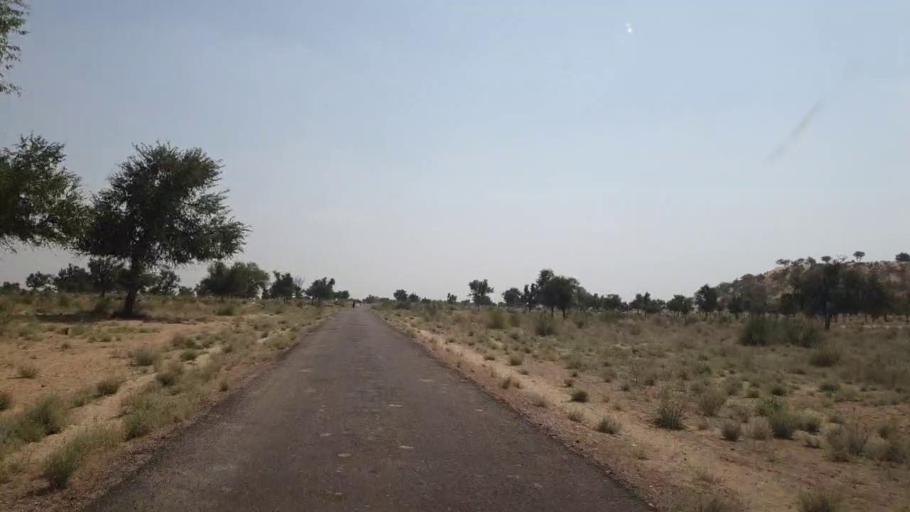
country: PK
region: Sindh
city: Islamkot
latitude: 25.1017
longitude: 70.7250
